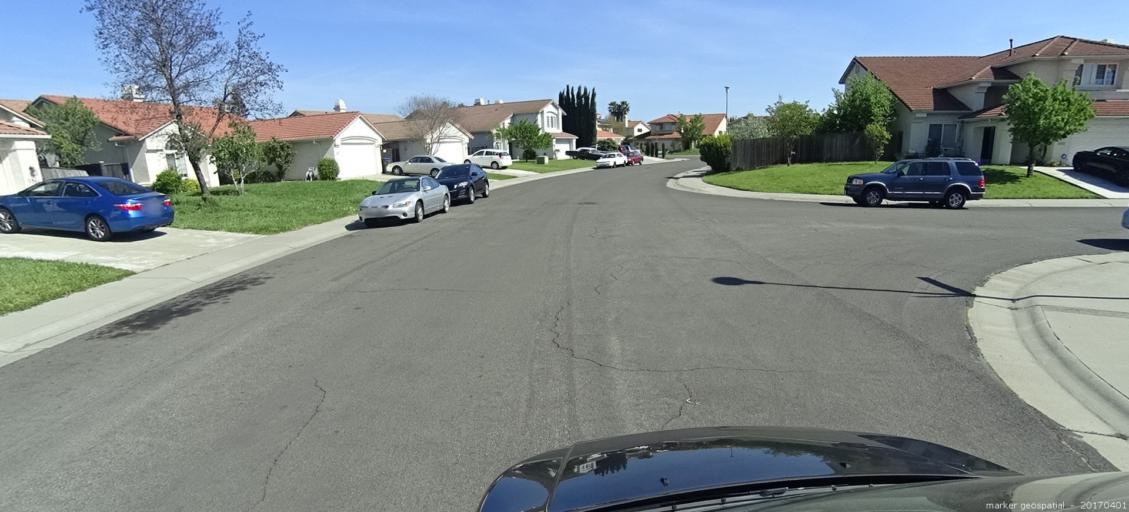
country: US
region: California
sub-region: Sacramento County
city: Laguna
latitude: 38.4453
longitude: -121.4395
